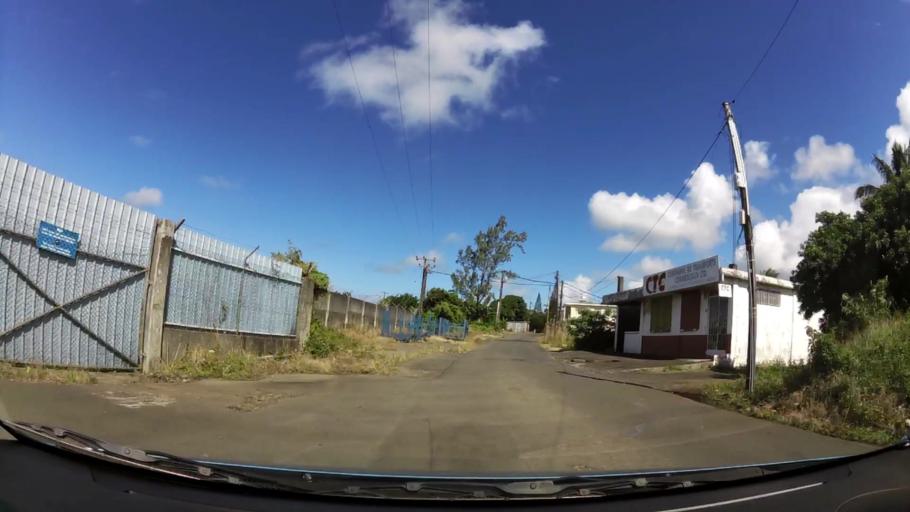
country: MU
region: Grand Port
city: Plaine Magnien
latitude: -20.4287
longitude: 57.6713
